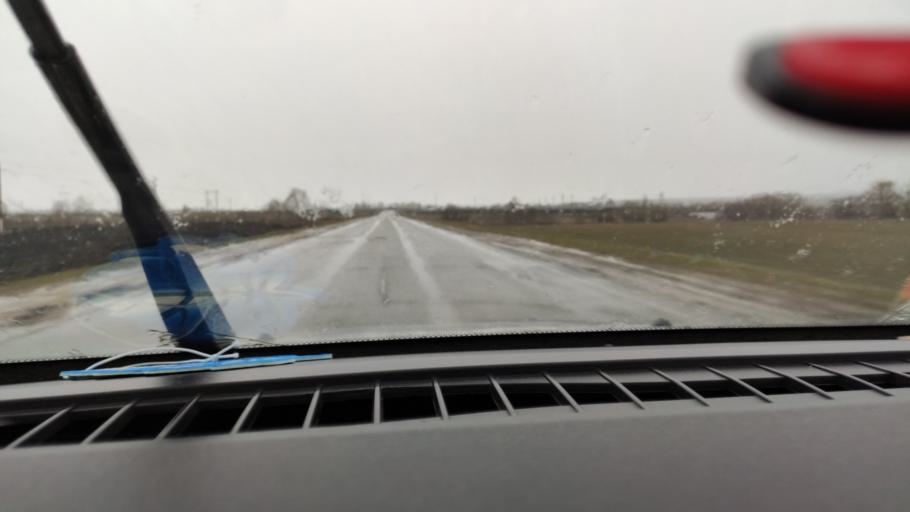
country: RU
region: Samara
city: Chelno-Vershiny
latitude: 54.7082
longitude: 51.1800
